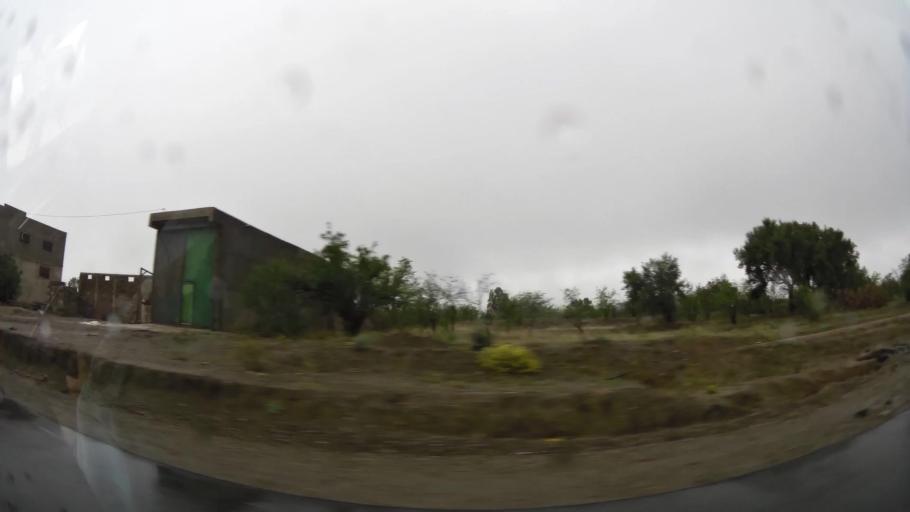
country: MA
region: Oriental
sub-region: Nador
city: Midar
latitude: 34.8458
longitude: -3.7215
